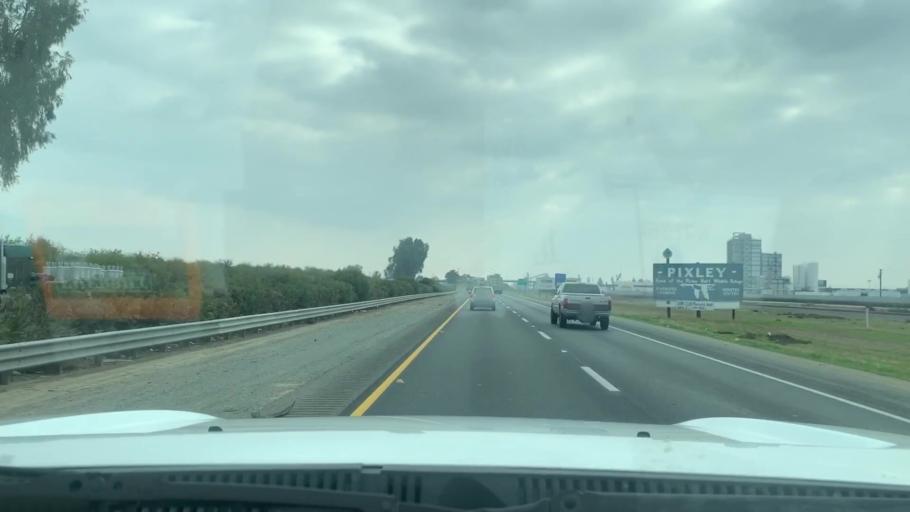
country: US
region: California
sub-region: Tulare County
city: Tipton
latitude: 36.0145
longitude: -119.3040
